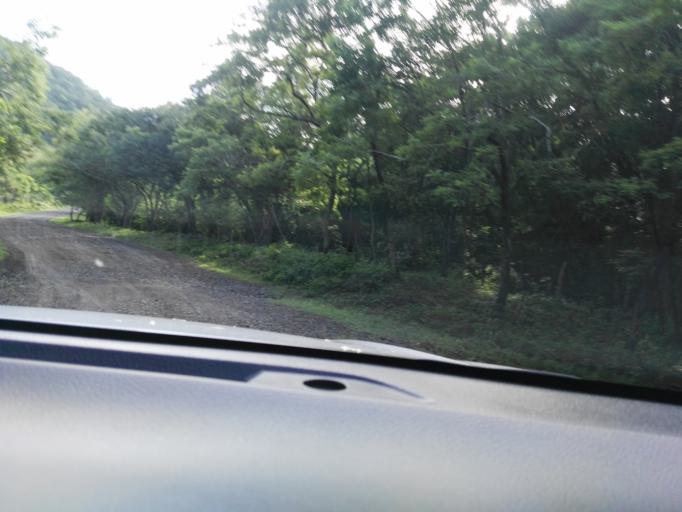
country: NI
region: Matagalpa
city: Terrabona
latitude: 12.8486
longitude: -86.0417
